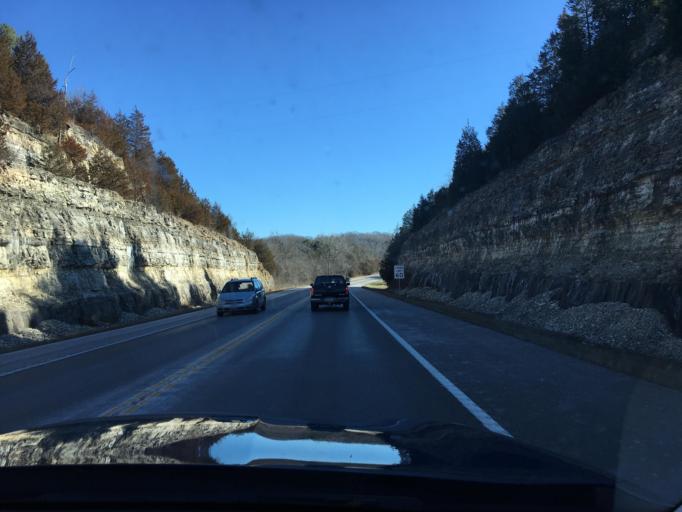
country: US
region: Missouri
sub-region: Jefferson County
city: De Soto
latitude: 38.1388
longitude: -90.4898
